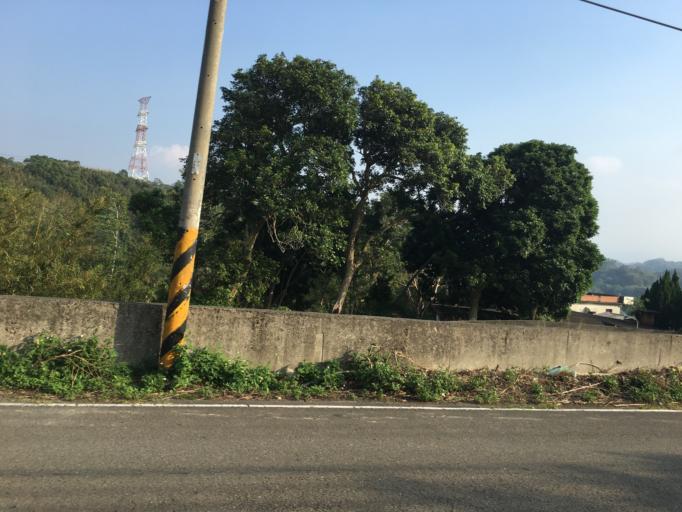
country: TW
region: Taiwan
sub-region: Hsinchu
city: Hsinchu
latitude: 24.7399
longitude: 121.0275
